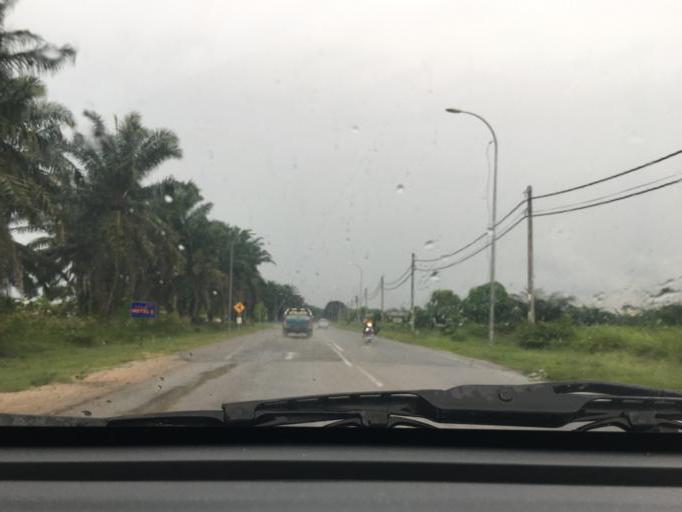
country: MY
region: Kedah
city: Sungai Petani
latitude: 5.5915
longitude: 100.6394
